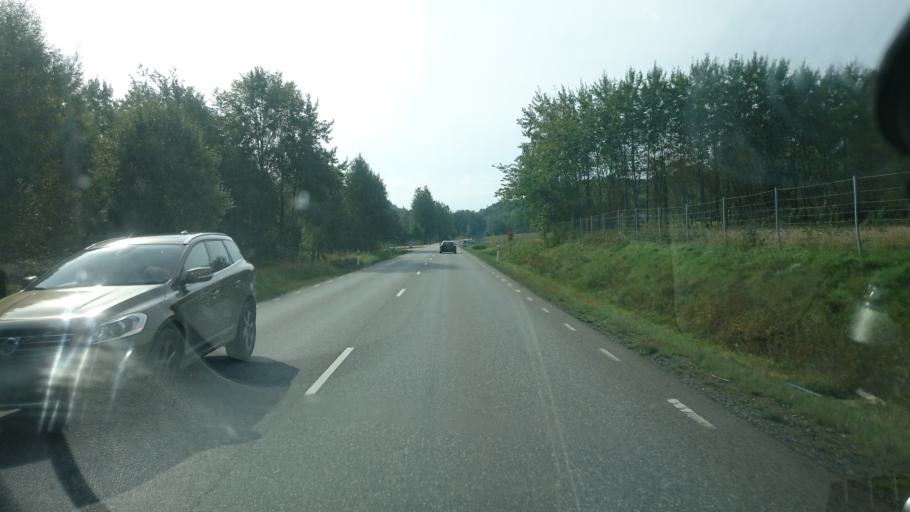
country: SE
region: Vaestra Goetaland
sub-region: Alingsas Kommun
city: Alingsas
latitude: 57.9909
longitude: 12.4412
